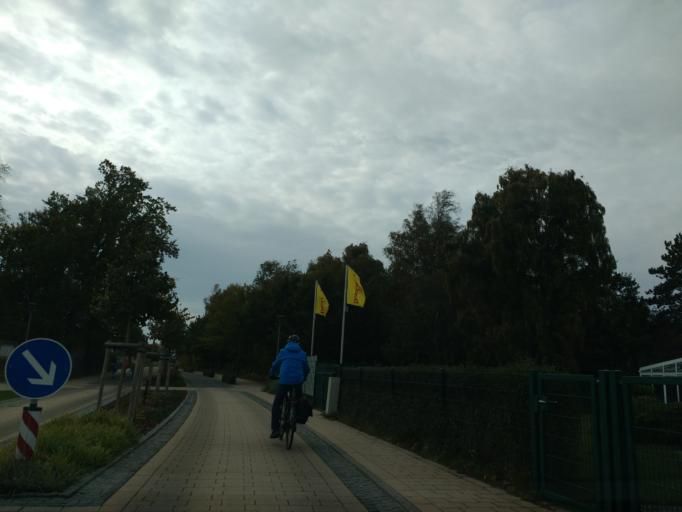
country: DE
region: Schleswig-Holstein
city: Gromitz
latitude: 54.1589
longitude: 10.9966
